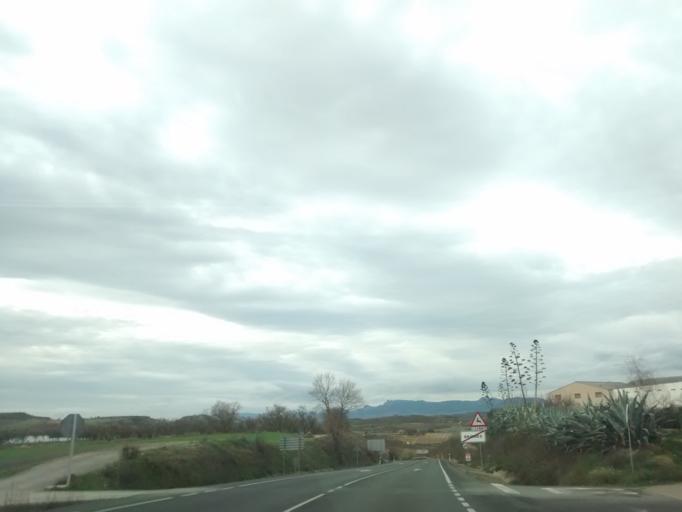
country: ES
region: La Rioja
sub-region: Provincia de La Rioja
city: Briones
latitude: 42.5423
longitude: -2.7889
